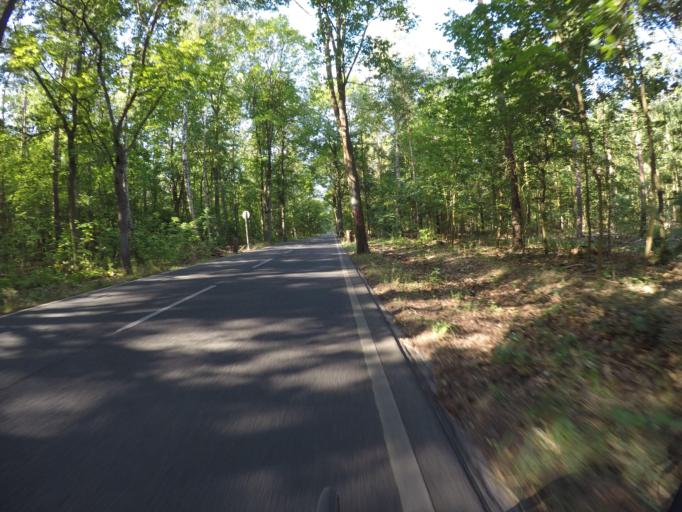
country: DE
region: Berlin
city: Schmockwitz
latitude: 52.3647
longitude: 13.6543
